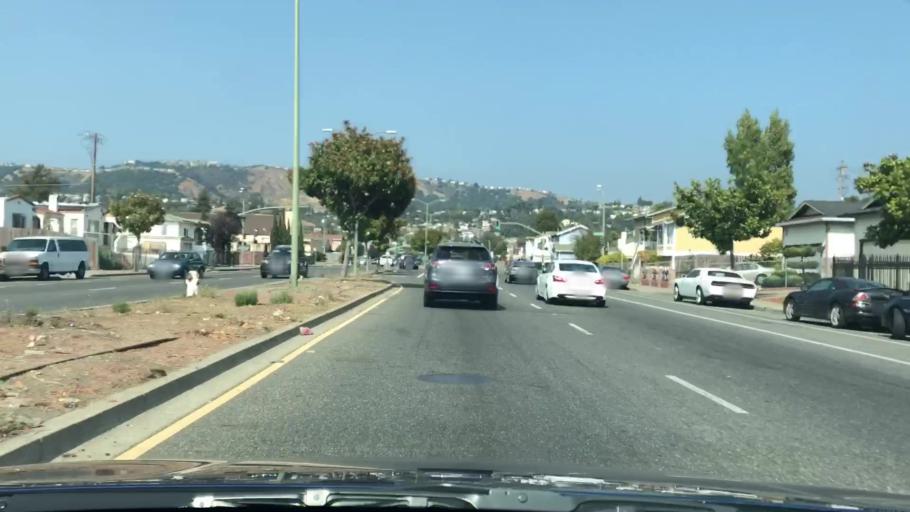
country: US
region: California
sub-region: Alameda County
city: San Leandro
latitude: 37.7631
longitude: -122.1811
